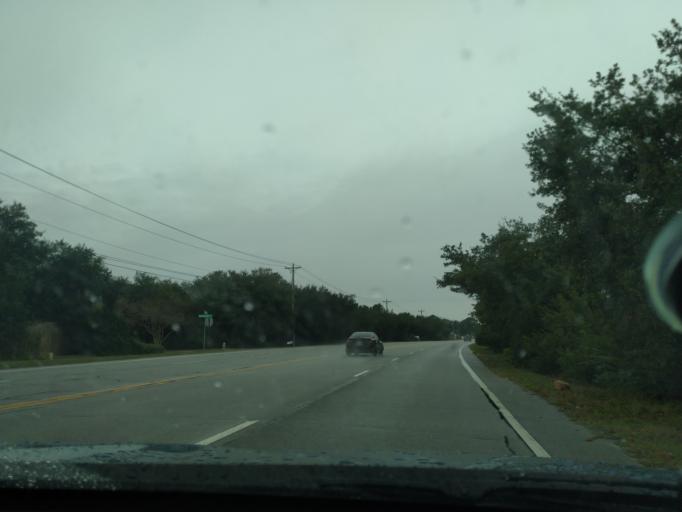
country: US
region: South Carolina
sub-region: Charleston County
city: Folly Beach
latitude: 32.6891
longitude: -79.9620
